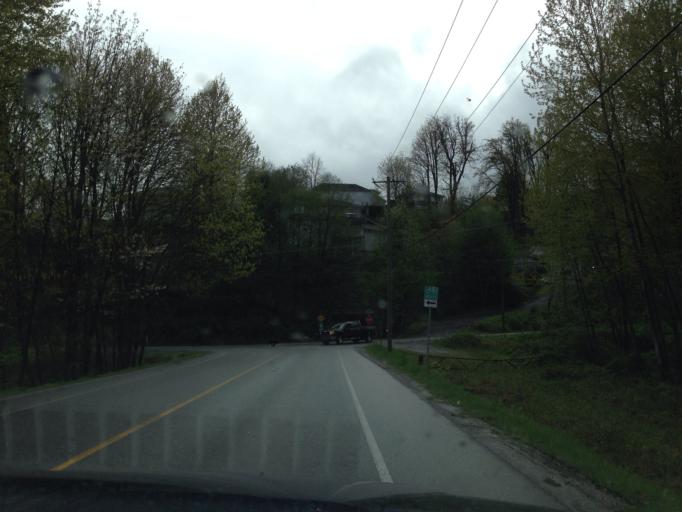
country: CA
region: British Columbia
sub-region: Fraser Valley Regional District
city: Chilliwack
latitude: 49.1623
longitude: -121.9944
